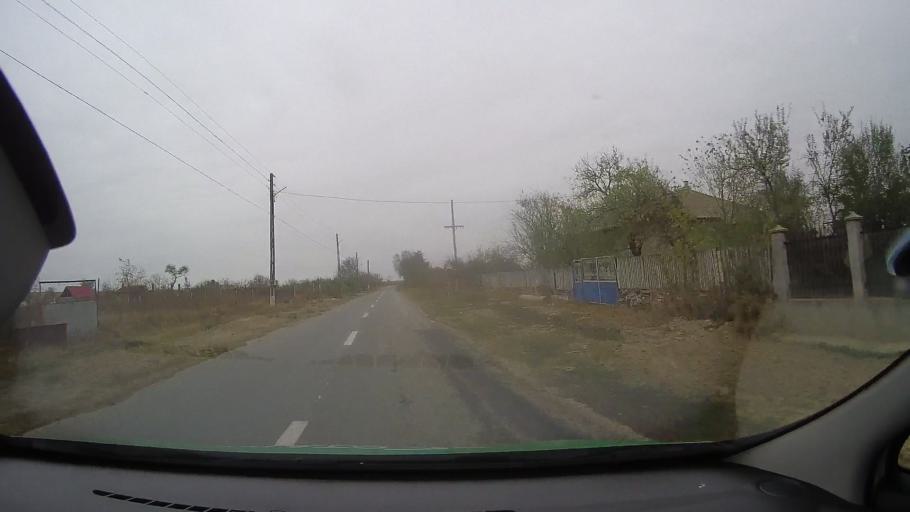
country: RO
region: Constanta
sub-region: Comuna Vulturu
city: Vulturu
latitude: 44.6547
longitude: 28.2673
